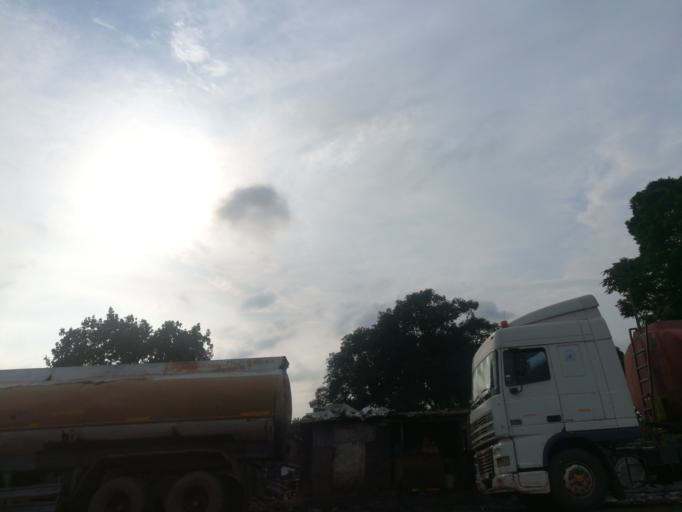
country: NG
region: Rivers
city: Okrika
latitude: 4.7741
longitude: 7.1070
